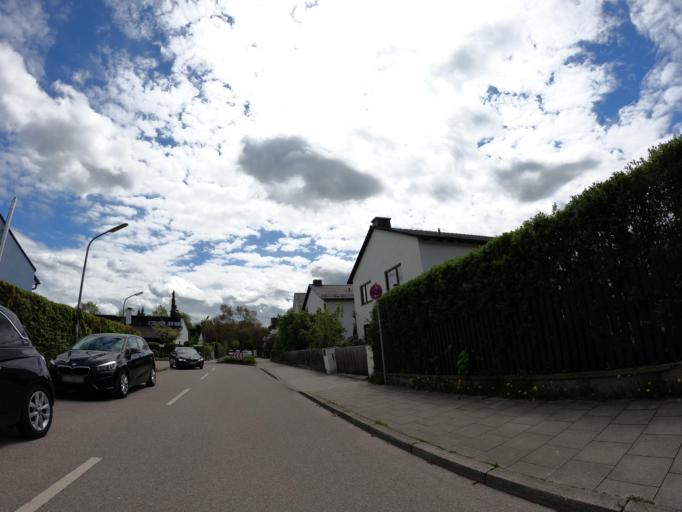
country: DE
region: Bavaria
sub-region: Upper Bavaria
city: Ottobrunn
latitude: 48.0685
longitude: 11.6778
